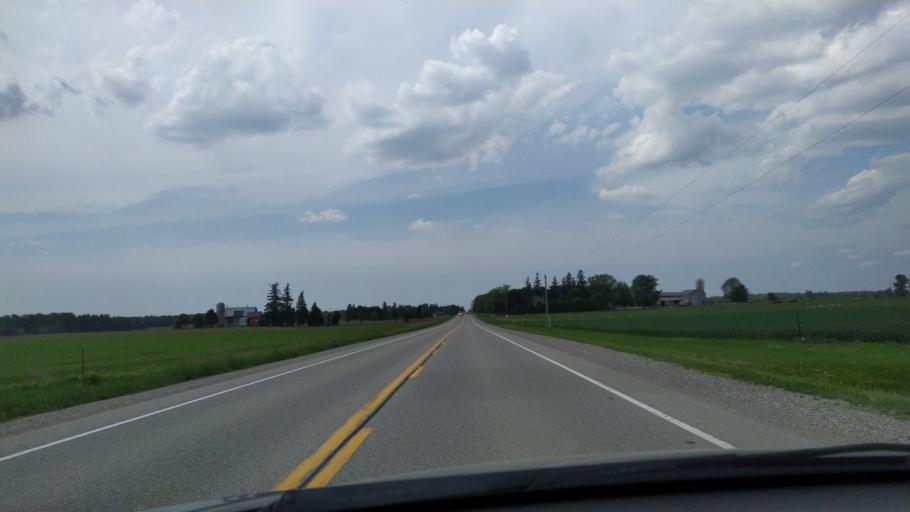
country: CA
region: Ontario
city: Dorchester
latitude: 43.1807
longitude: -81.0513
